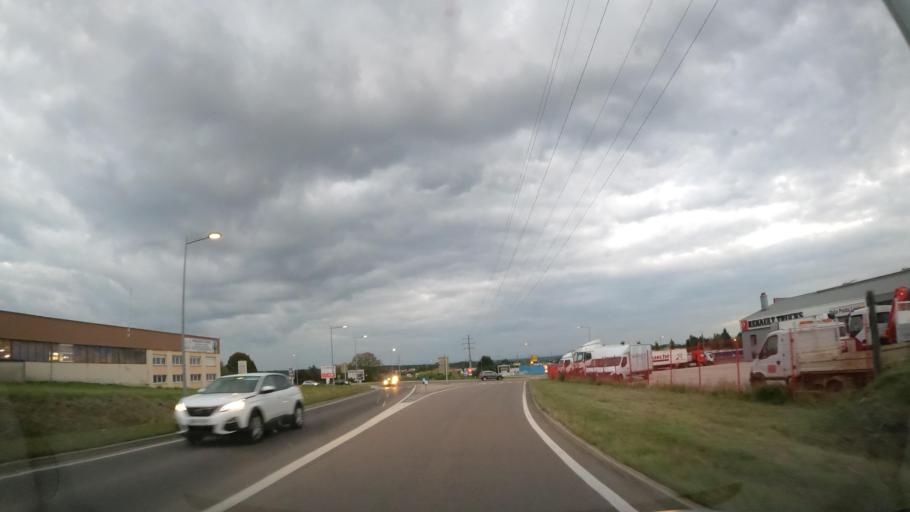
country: FR
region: Franche-Comte
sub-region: Departement du Jura
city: Dole
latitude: 47.1104
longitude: 5.4989
